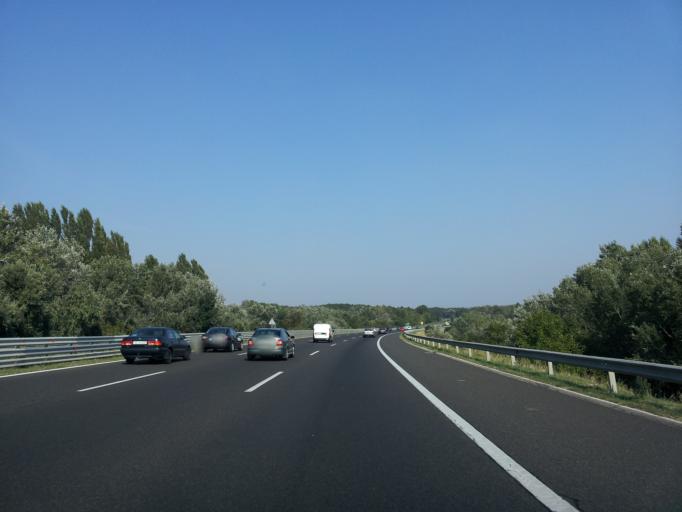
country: HU
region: Fejer
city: Gardony
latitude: 47.2320
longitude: 18.5869
